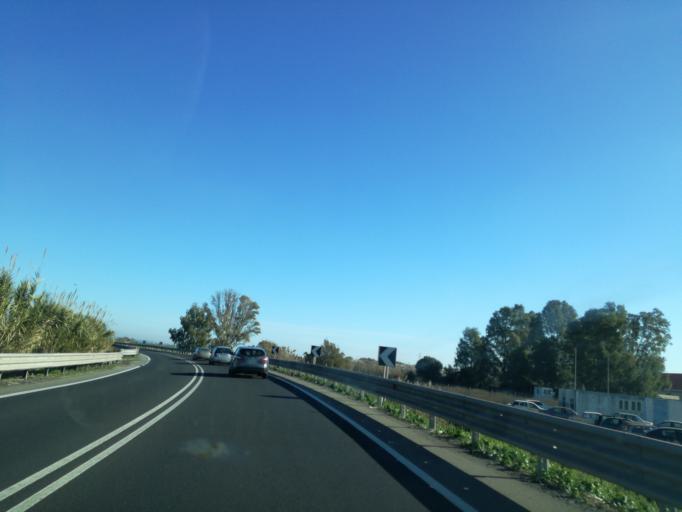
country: IT
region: Sicily
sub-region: Catania
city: Motta Sant'Anastasia
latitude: 37.4109
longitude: 14.9055
